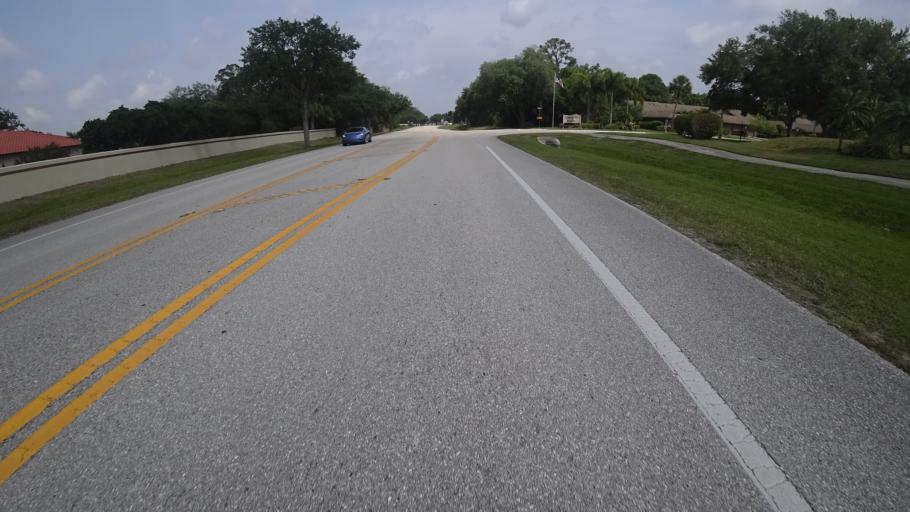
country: US
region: Florida
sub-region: Sarasota County
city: Desoto Lakes
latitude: 27.4123
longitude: -82.4896
